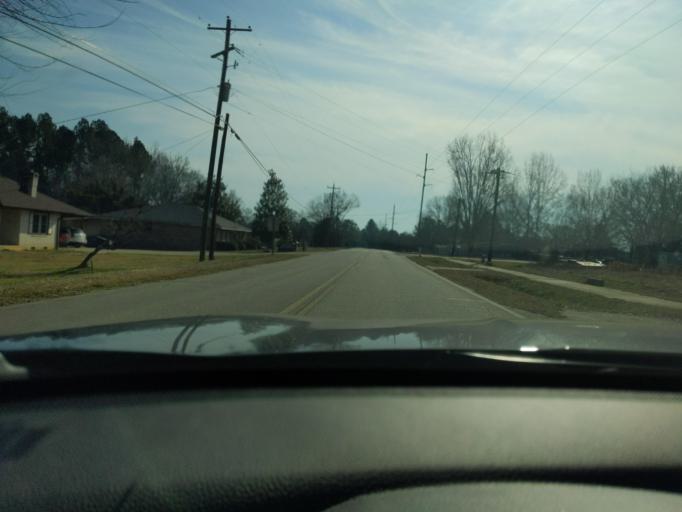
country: US
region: South Carolina
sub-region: Abbeville County
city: Calhoun Falls
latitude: 34.0867
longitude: -82.5852
